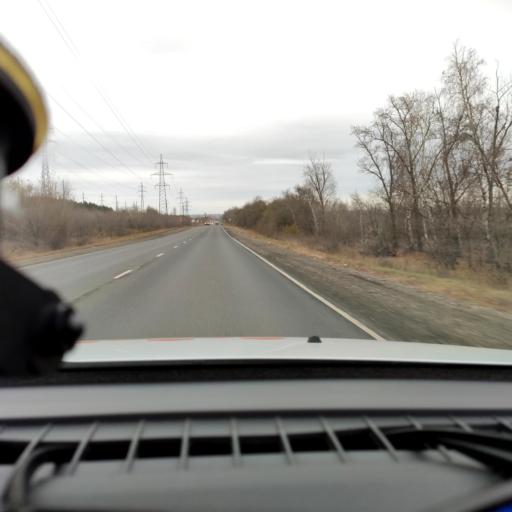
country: RU
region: Samara
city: Samara
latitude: 53.1208
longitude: 50.2136
